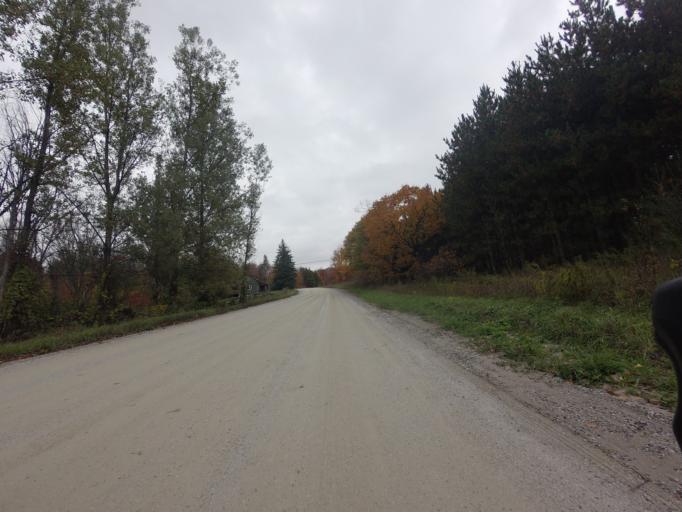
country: CA
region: Ontario
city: Renfrew
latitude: 45.1367
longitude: -76.6288
